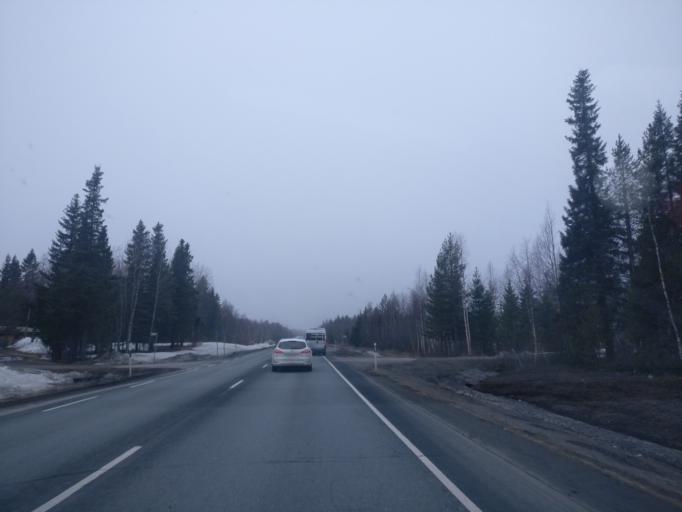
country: FI
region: Lapland
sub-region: Kemi-Tornio
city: Simo
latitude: 65.6748
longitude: 24.8842
